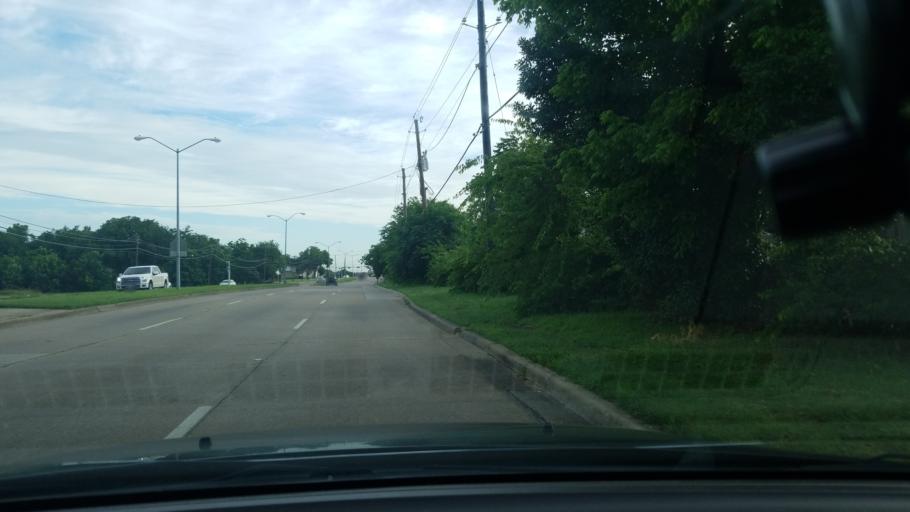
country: US
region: Texas
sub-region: Dallas County
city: Balch Springs
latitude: 32.7589
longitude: -96.6480
